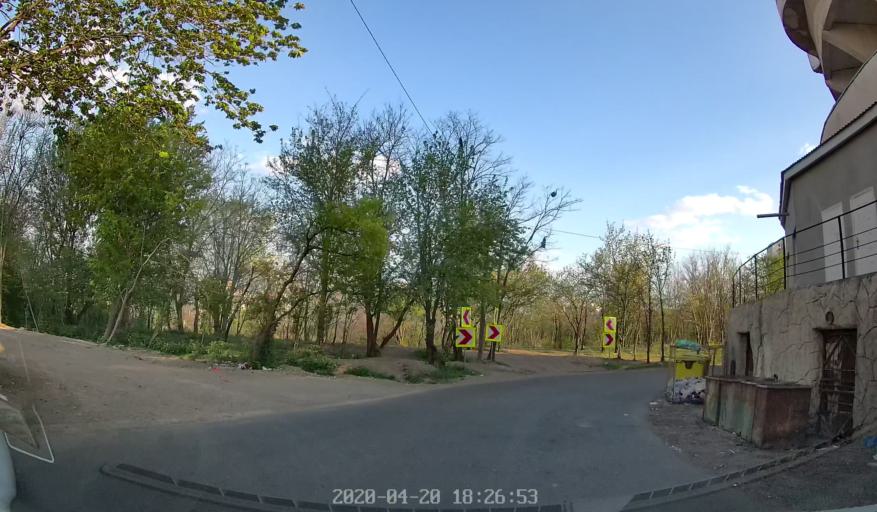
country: MD
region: Chisinau
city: Chisinau
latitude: 46.9909
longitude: 28.8377
